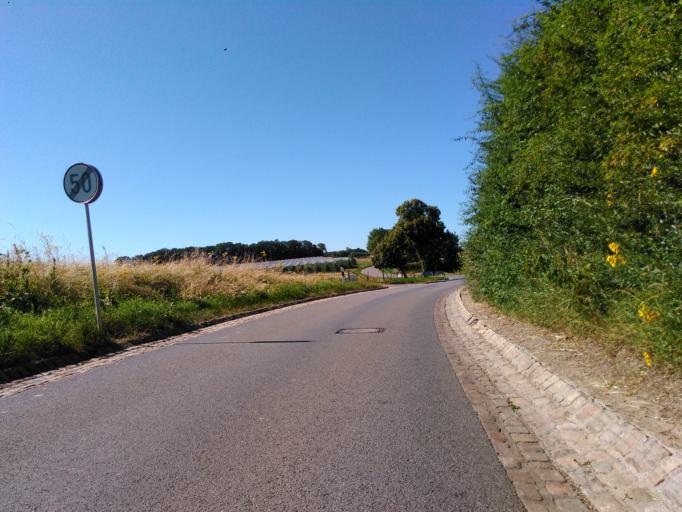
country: LU
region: Luxembourg
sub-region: Canton de Capellen
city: Dippach
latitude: 49.5608
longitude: 5.9770
